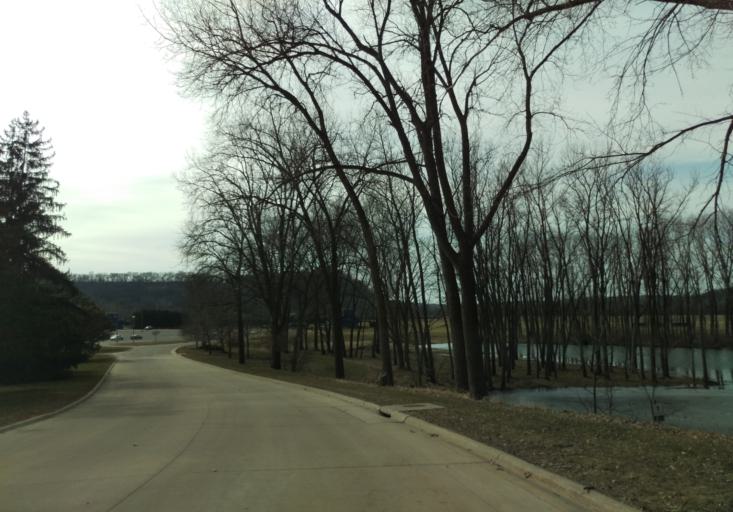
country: US
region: Iowa
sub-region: Winneshiek County
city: Decorah
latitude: 43.3163
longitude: -91.8049
